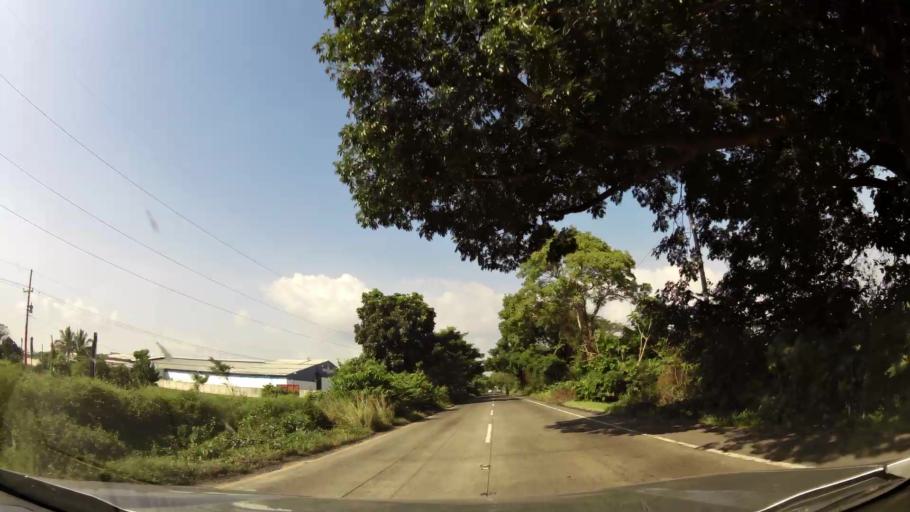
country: GT
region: Escuintla
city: Puerto San Jose
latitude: 13.9760
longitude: -90.7885
